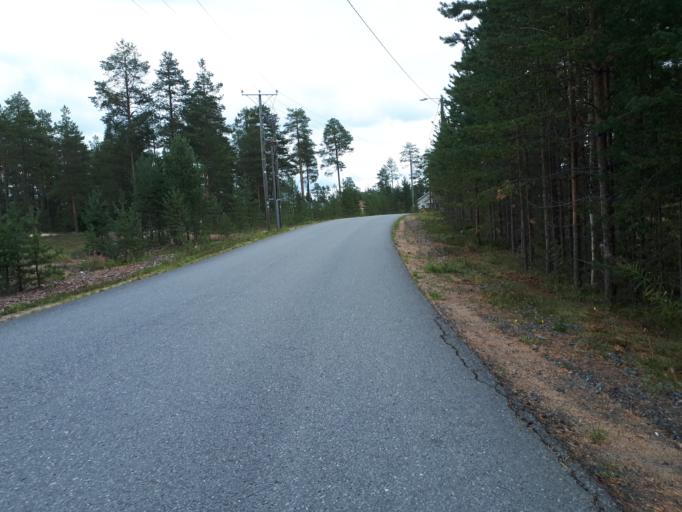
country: FI
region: Northern Ostrobothnia
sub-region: Oulunkaari
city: Ii
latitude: 65.3248
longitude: 25.4048
